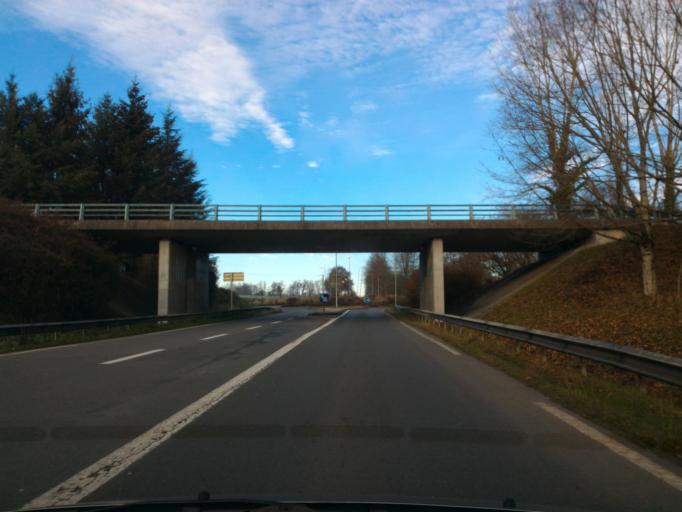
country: FR
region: Poitou-Charentes
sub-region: Departement de la Charente
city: Confolens
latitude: 46.0234
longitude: 0.6541
